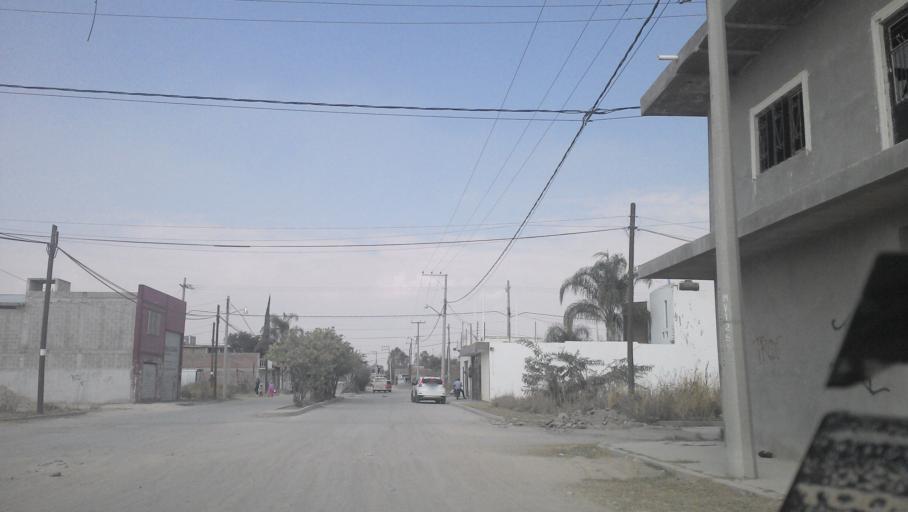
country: MX
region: Guanajuato
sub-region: San Francisco del Rincon
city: Fraccionamiento Villa Jardin
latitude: 21.0005
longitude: -101.8542
